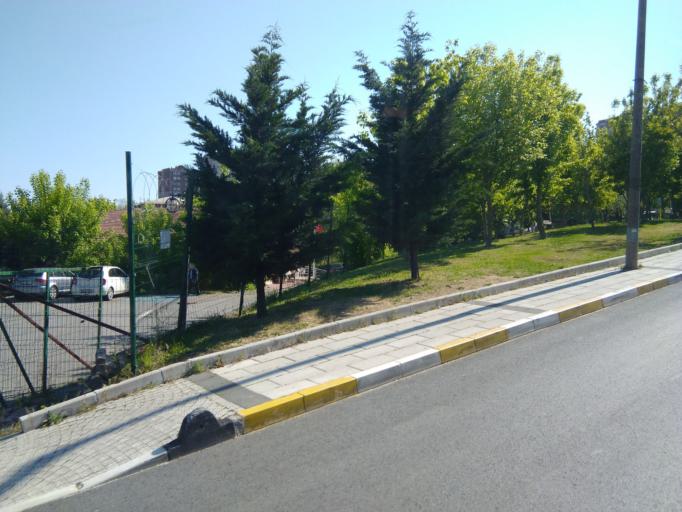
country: TR
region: Istanbul
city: Mahmutbey
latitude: 41.0461
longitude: 28.7961
